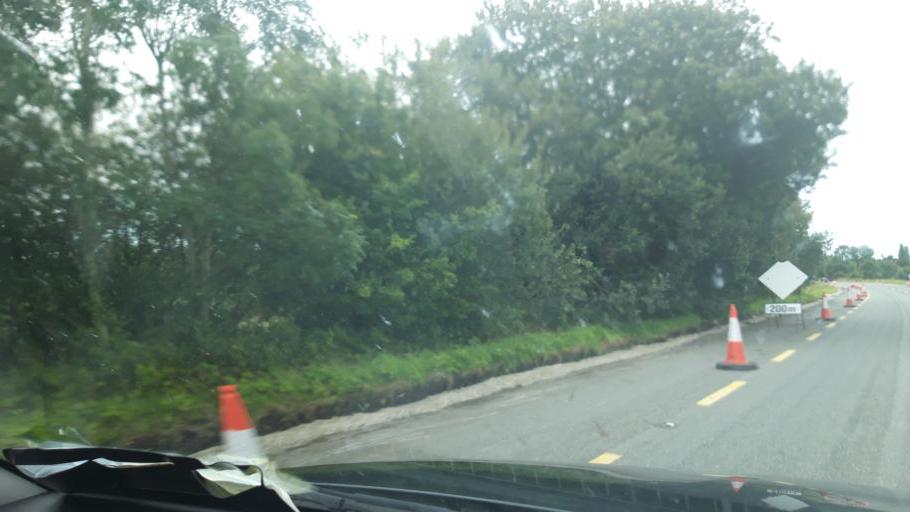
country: IE
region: Leinster
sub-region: Kilkenny
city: Kilkenny
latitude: 52.6085
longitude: -7.2958
